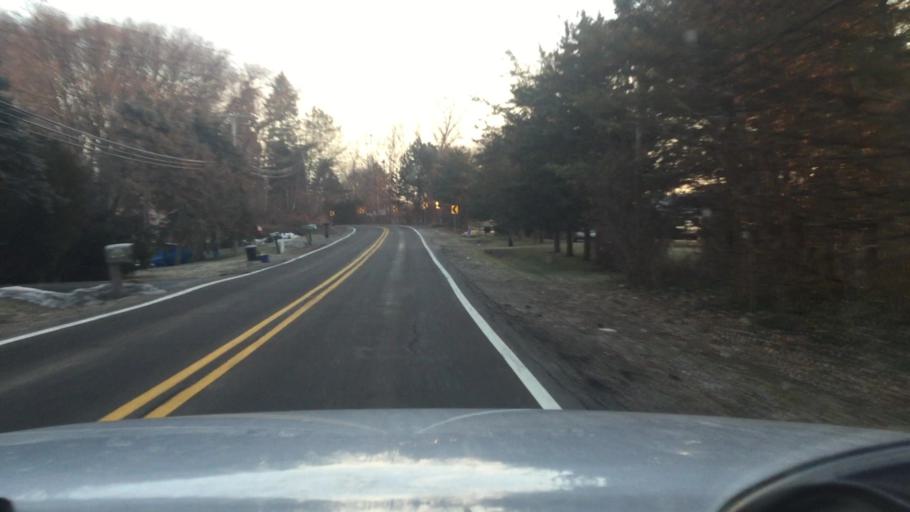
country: US
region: Michigan
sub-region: Oakland County
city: Waterford
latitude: 42.6692
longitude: -83.3587
